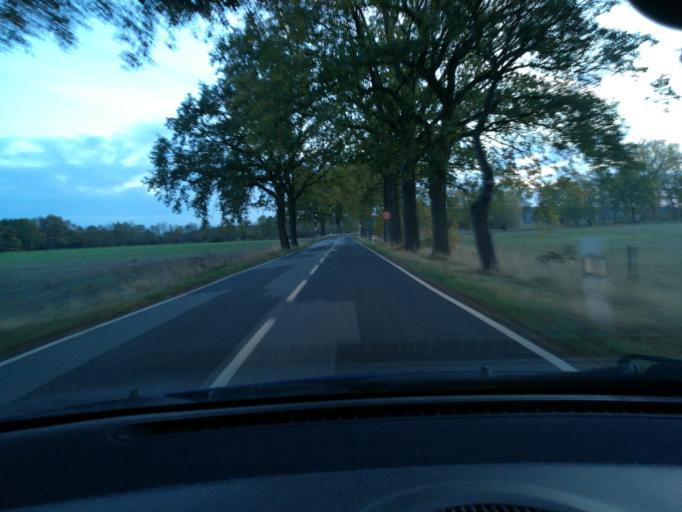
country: DE
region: Brandenburg
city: Lenzen
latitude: 53.0864
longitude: 11.4663
